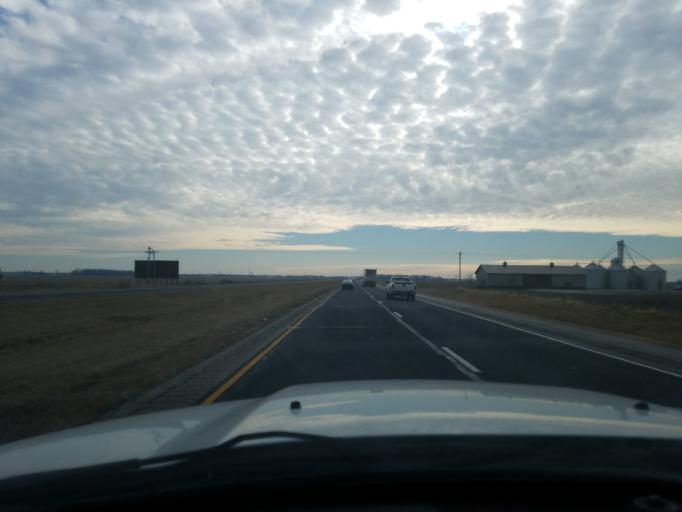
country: US
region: Indiana
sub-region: Huntington County
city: Markle
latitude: 40.8612
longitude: -85.3449
